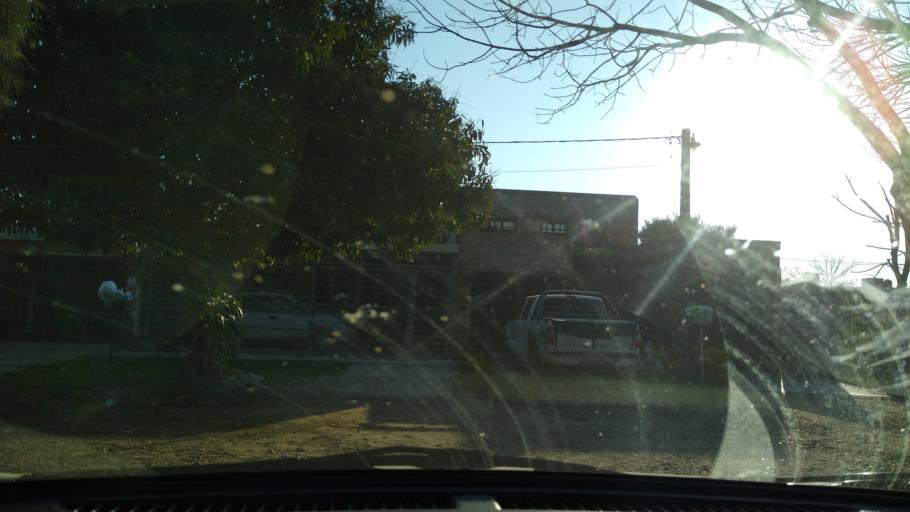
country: AR
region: Chaco
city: Resistencia
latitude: -27.4812
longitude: -58.9731
